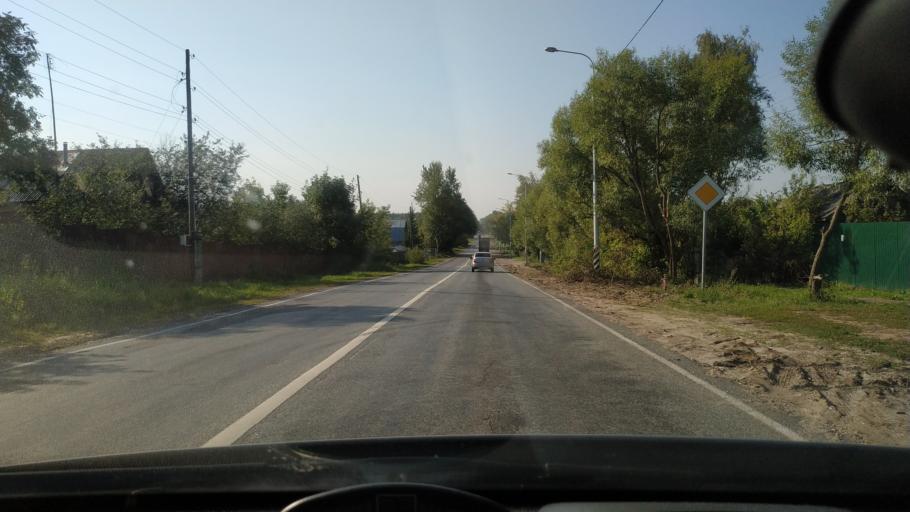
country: RU
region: Moskovskaya
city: Tugolesskiy Bor
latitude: 55.5228
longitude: 39.7109
